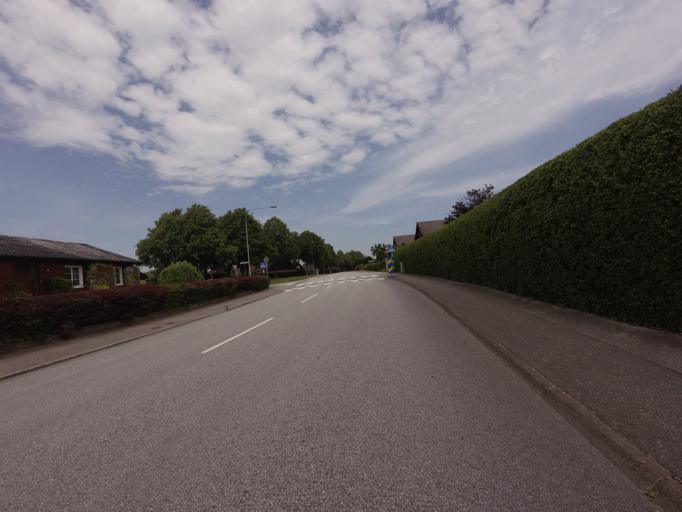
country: SE
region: Skane
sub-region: Ystads Kommun
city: Ystad
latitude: 55.4275
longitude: 13.7977
